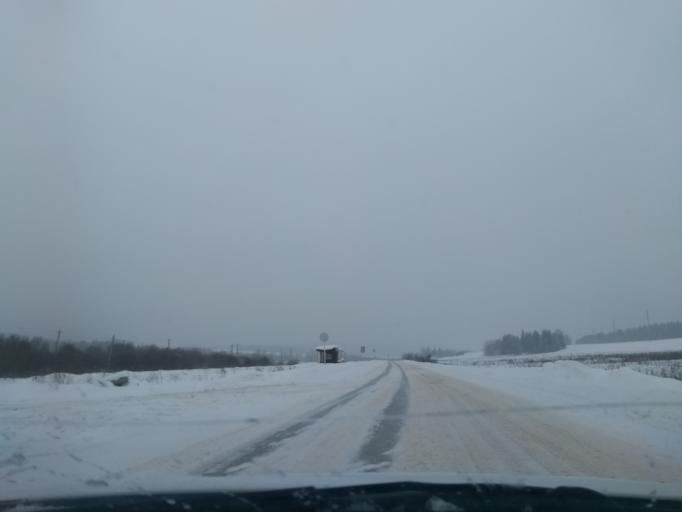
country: RU
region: Perm
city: Sylva
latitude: 57.8325
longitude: 56.6669
